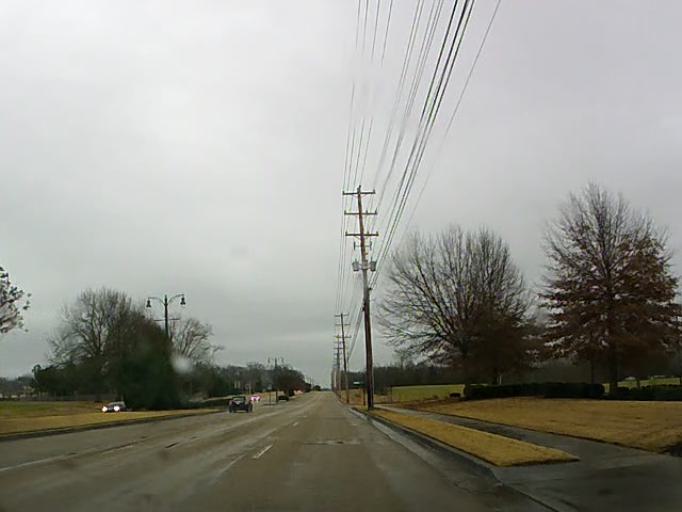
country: US
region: Tennessee
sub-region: Shelby County
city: Germantown
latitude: 35.0475
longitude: -89.7563
